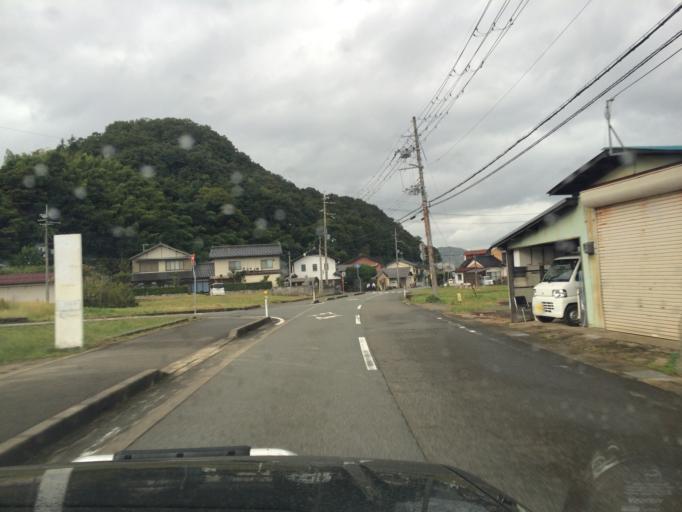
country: JP
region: Hyogo
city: Toyooka
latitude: 35.4715
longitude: 134.7740
